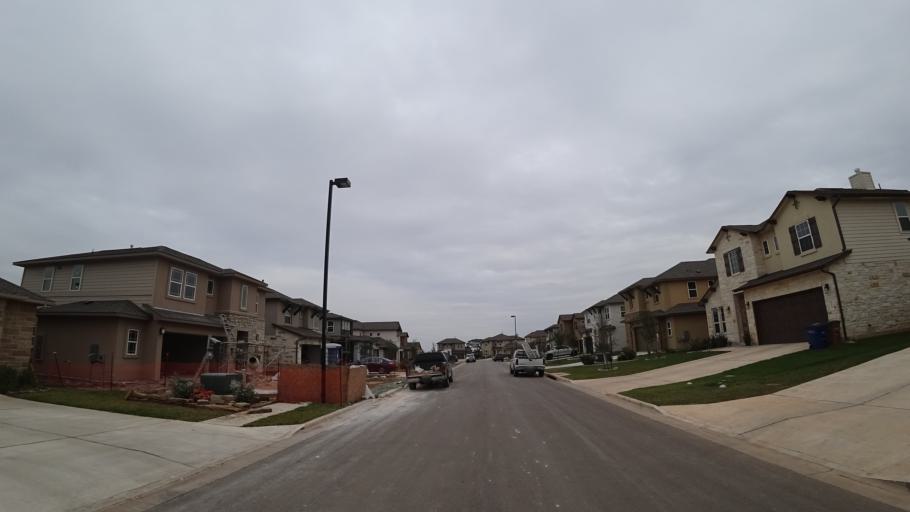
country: US
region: Texas
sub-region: Travis County
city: Shady Hollow
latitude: 30.1672
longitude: -97.8876
